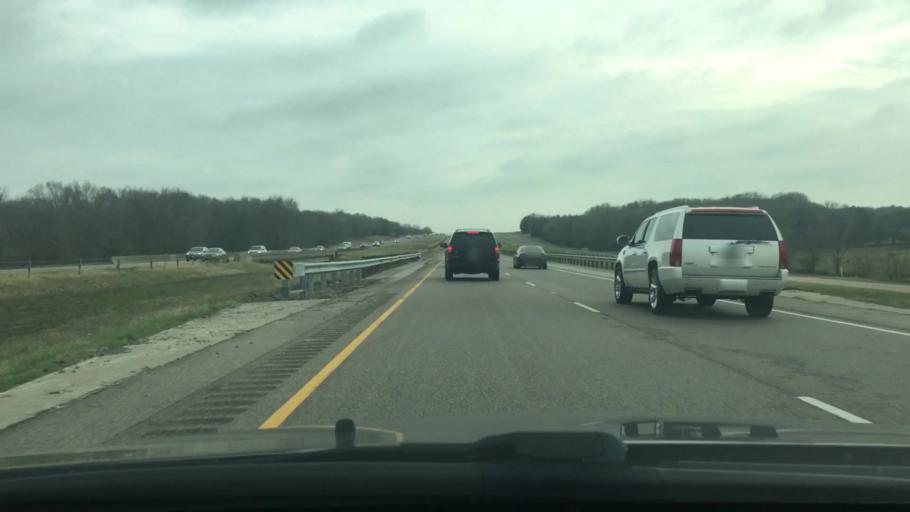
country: US
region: Texas
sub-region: Freestone County
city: Fairfield
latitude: 31.6480
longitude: -96.1598
